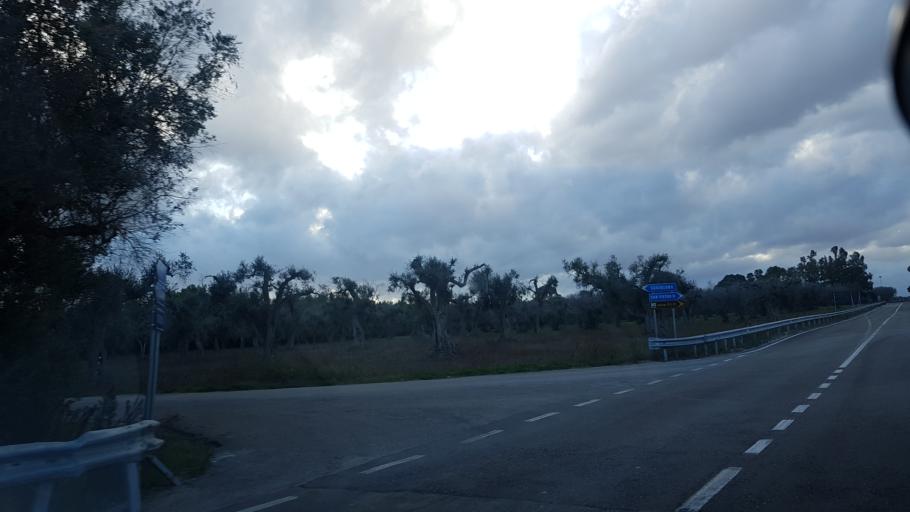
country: IT
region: Apulia
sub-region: Provincia di Brindisi
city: Torchiarolo
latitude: 40.4871
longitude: 18.0295
